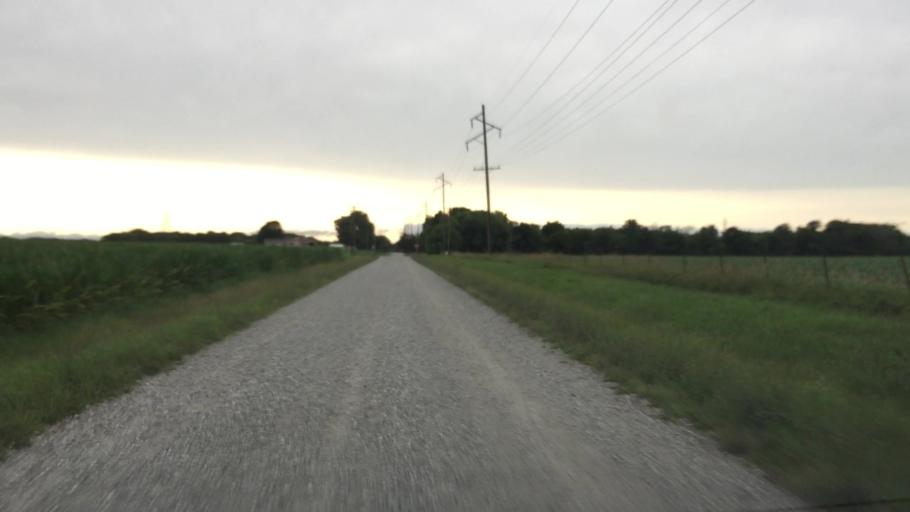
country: US
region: Illinois
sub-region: Hancock County
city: Hamilton
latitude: 40.4265
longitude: -91.3474
